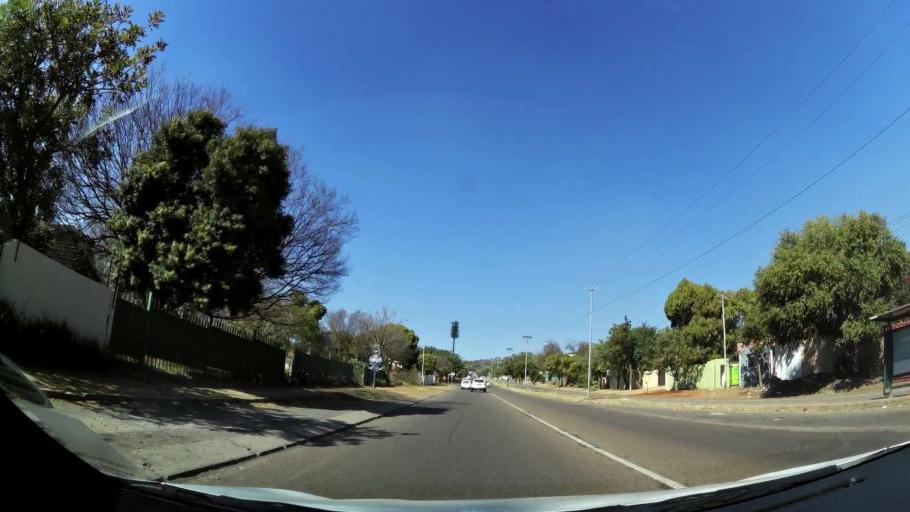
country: ZA
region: Gauteng
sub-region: City of Tshwane Metropolitan Municipality
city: Pretoria
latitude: -25.7755
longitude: 28.2255
